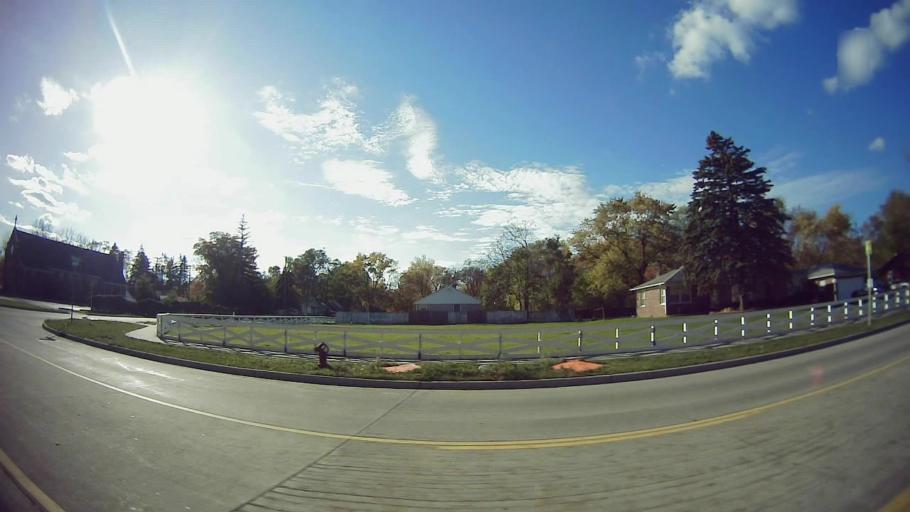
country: US
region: Michigan
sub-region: Oakland County
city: Southfield
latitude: 42.4467
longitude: -83.2394
